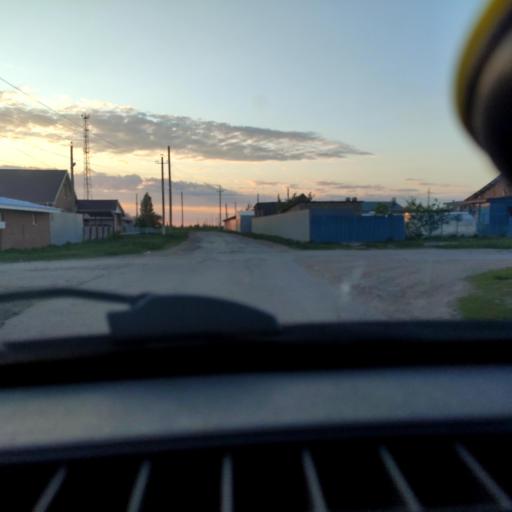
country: RU
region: Samara
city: Povolzhskiy
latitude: 53.6444
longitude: 49.6839
